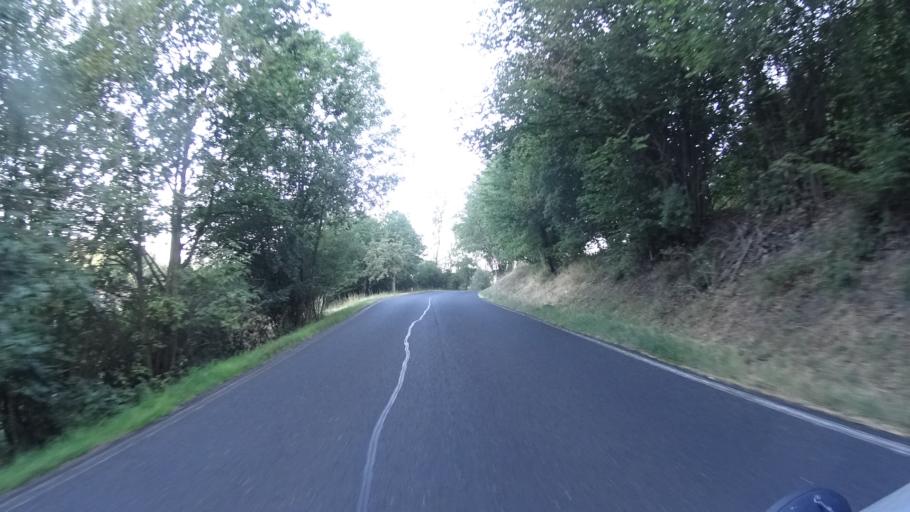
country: CZ
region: Ustecky
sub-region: Okres Litomerice
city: Litomerice
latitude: 50.5766
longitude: 14.0909
